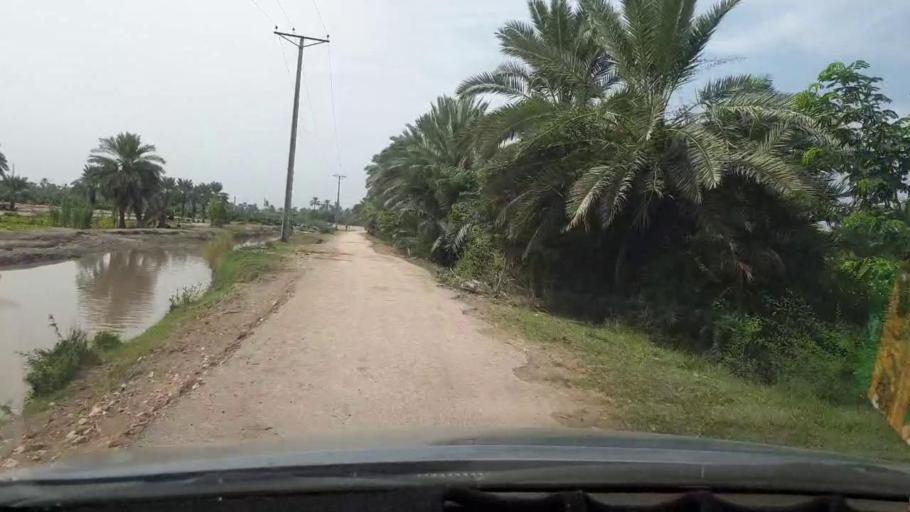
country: PK
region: Sindh
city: Khairpur
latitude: 27.5075
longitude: 68.7566
